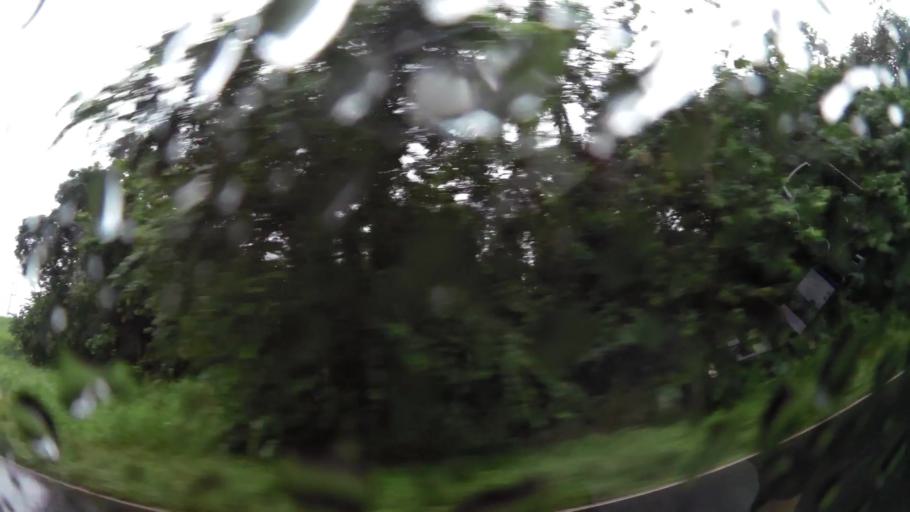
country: PA
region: Panama
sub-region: Distrito de Panama
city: Paraiso
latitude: 9.0049
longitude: -79.5911
